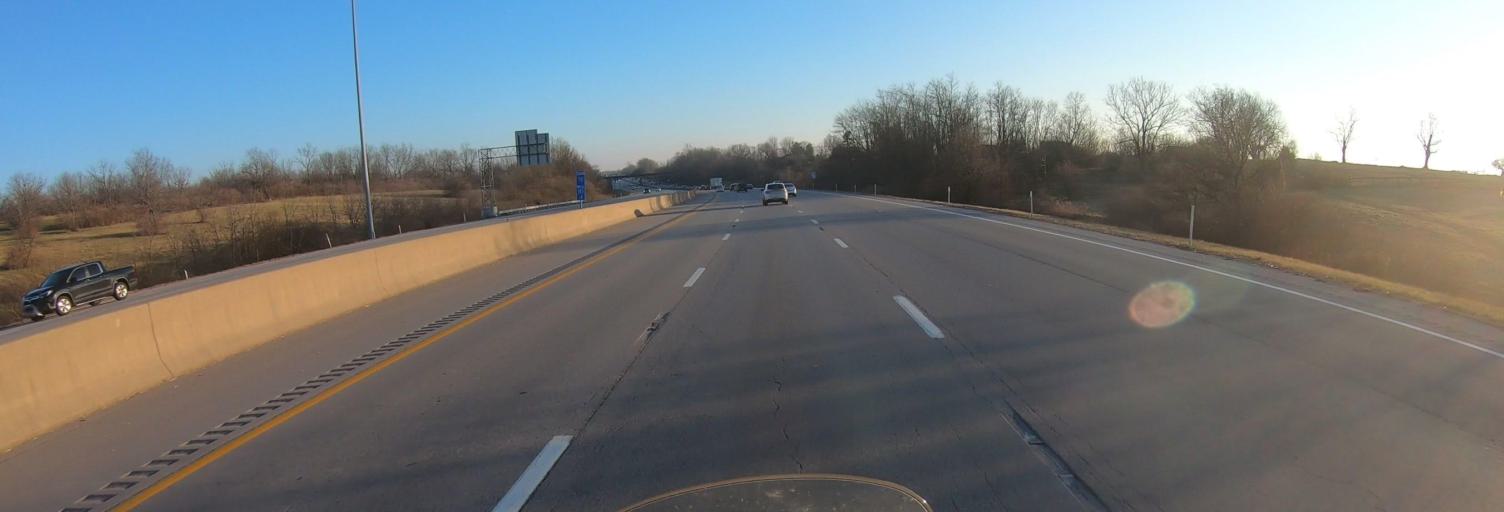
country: US
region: Kentucky
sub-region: Fayette County
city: Lexington
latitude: 37.9547
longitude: -84.3886
